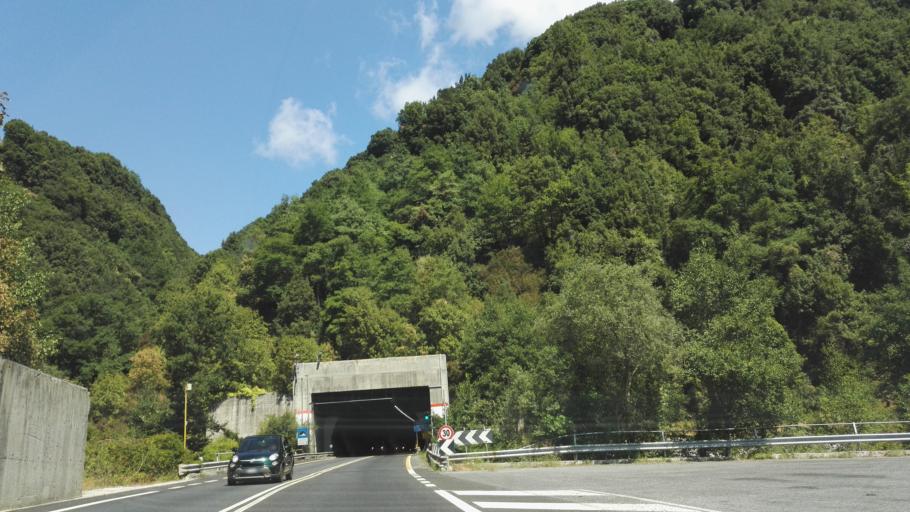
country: IT
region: Calabria
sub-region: Provincia di Reggio Calabria
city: Amato
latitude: 38.3745
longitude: 16.1776
